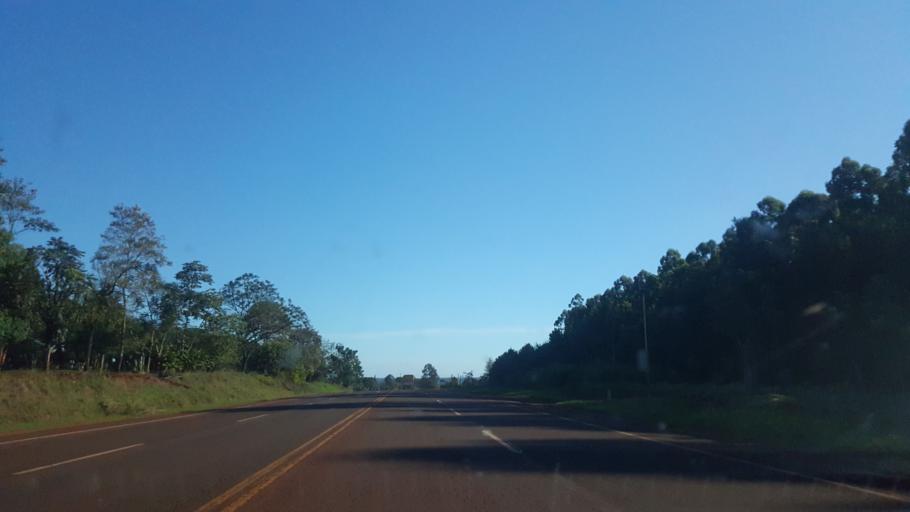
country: AR
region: Misiones
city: Puerto Esperanza
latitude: -26.1763
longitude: -54.5882
